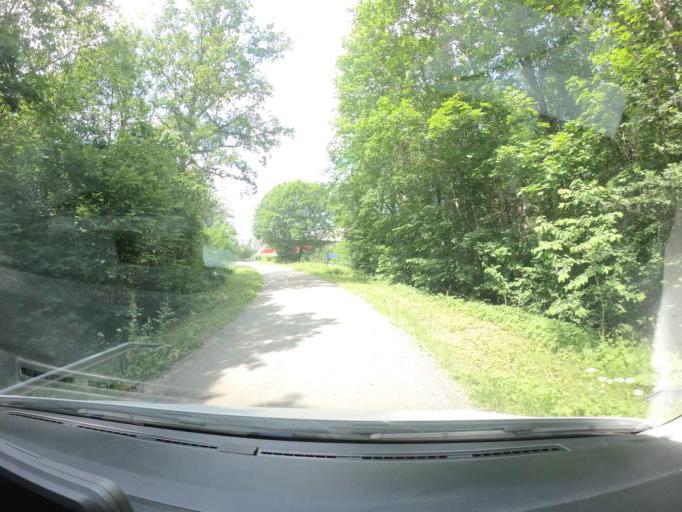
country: SE
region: Skane
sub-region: Hassleholms Kommun
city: Sosdala
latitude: 55.9815
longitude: 13.6488
